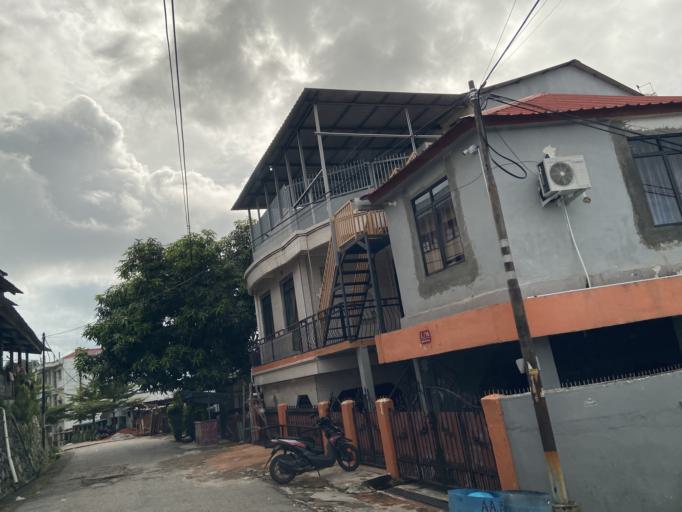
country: SG
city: Singapore
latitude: 1.1308
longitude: 104.0141
